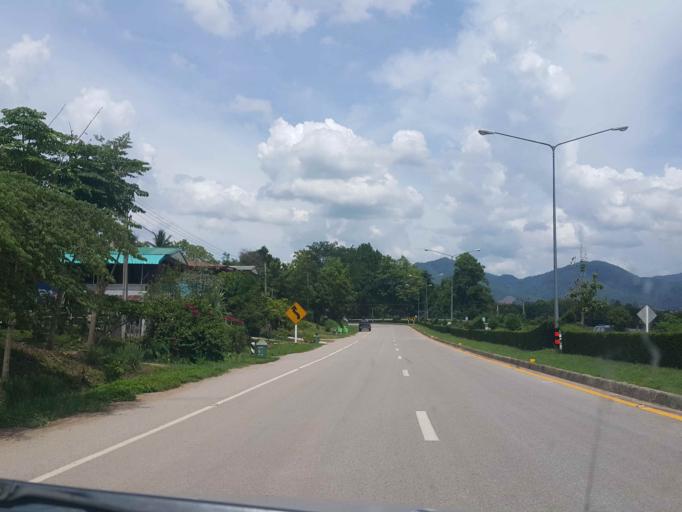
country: TH
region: Nan
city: Ban Luang
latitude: 18.8494
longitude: 100.4288
